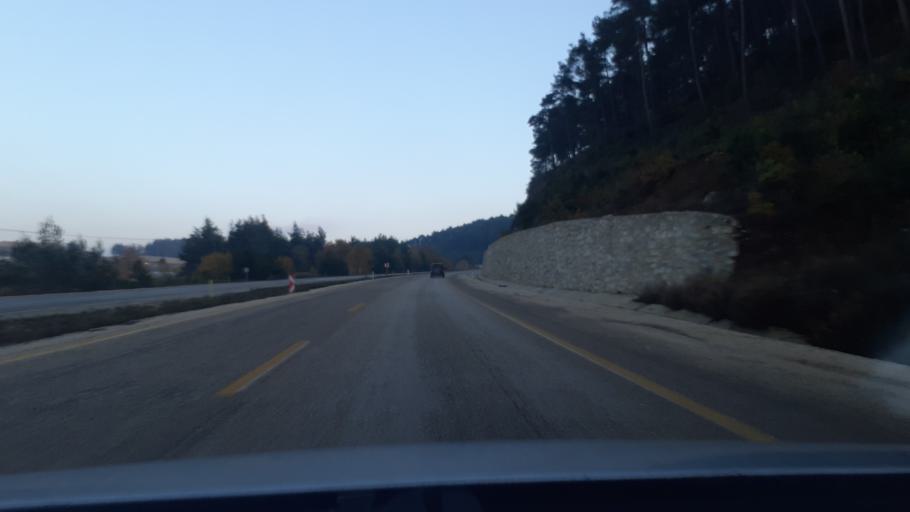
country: TR
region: Hatay
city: Yayladagi
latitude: 35.8943
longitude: 36.0826
